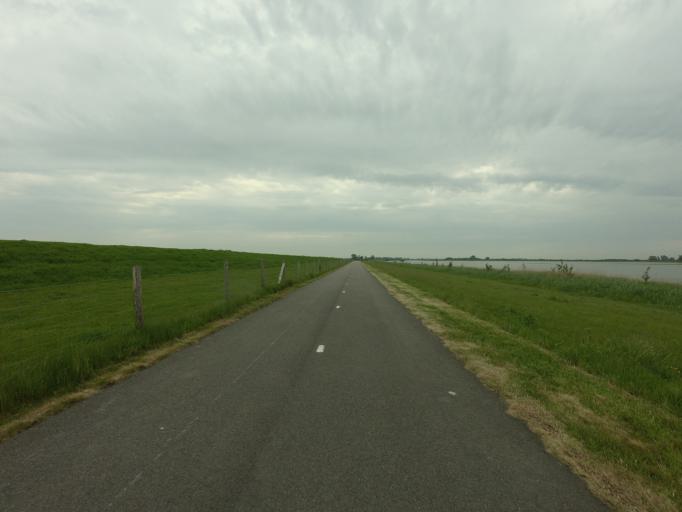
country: NL
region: South Holland
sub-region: Gemeente Goeree-Overflakkee
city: Middelharnis
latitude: 51.7977
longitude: 4.2388
